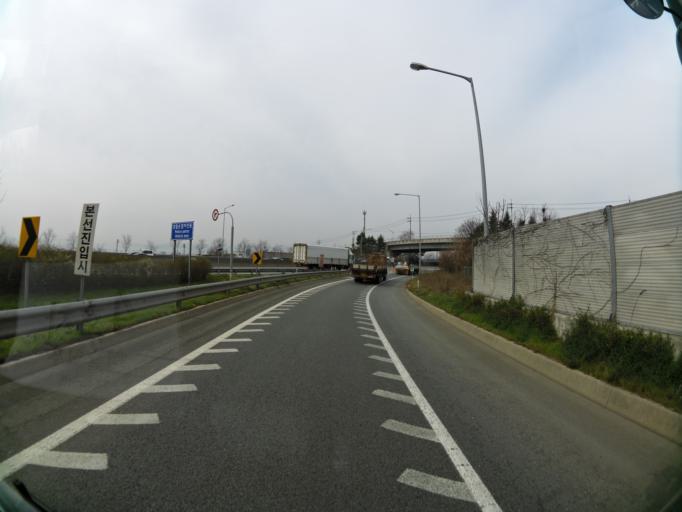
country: KR
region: Gyeongsangbuk-do
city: Hayang
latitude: 35.8776
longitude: 128.7855
